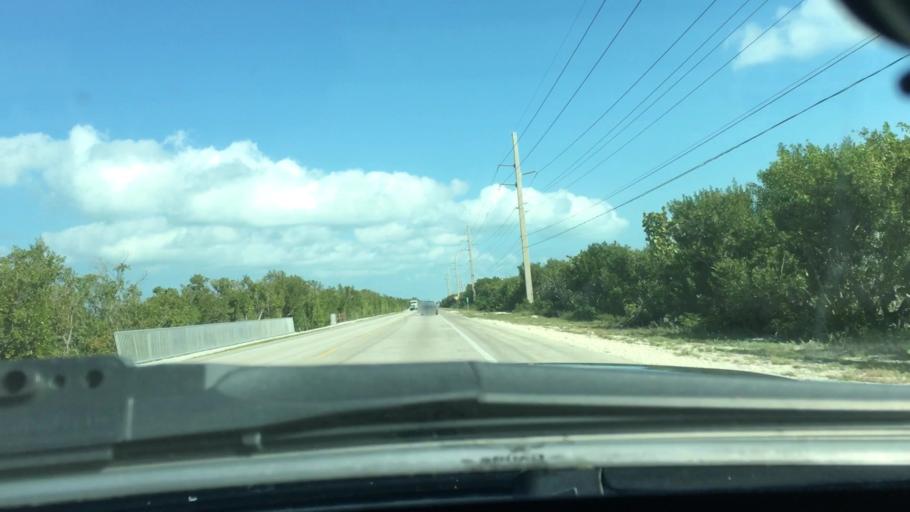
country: US
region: Florida
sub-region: Monroe County
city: Big Pine Key
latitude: 24.6667
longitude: -81.2585
